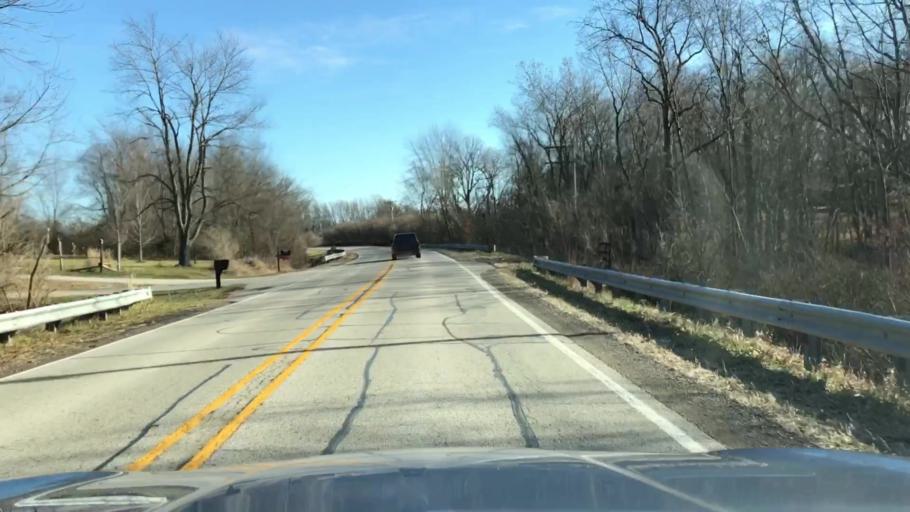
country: US
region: Illinois
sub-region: McLean County
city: Lexington
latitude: 40.6462
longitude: -88.8378
